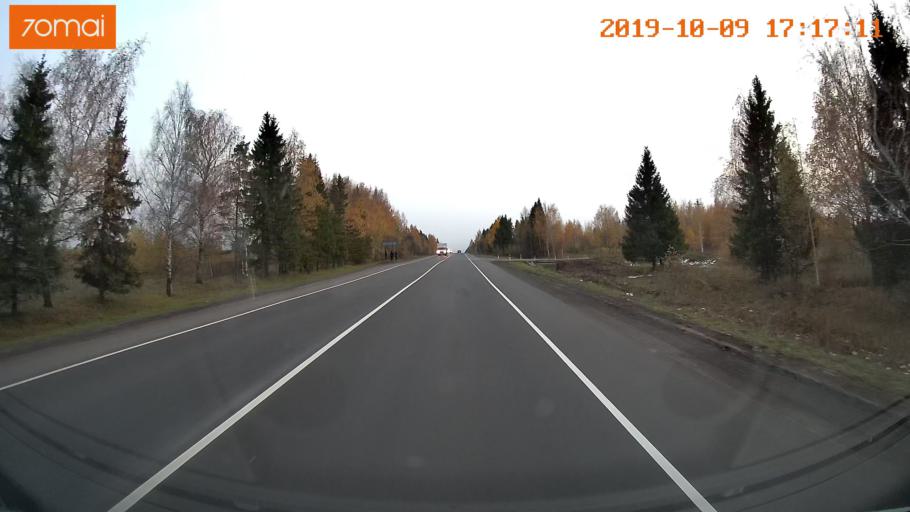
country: RU
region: Ivanovo
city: Furmanov
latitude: 57.2795
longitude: 41.1589
